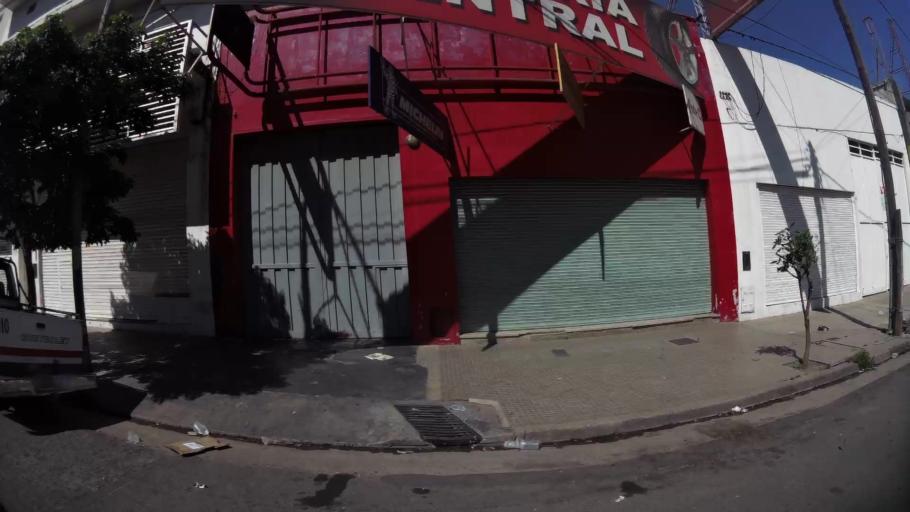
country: AR
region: Cordoba
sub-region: Departamento de Capital
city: Cordoba
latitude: -31.4084
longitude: -64.1732
